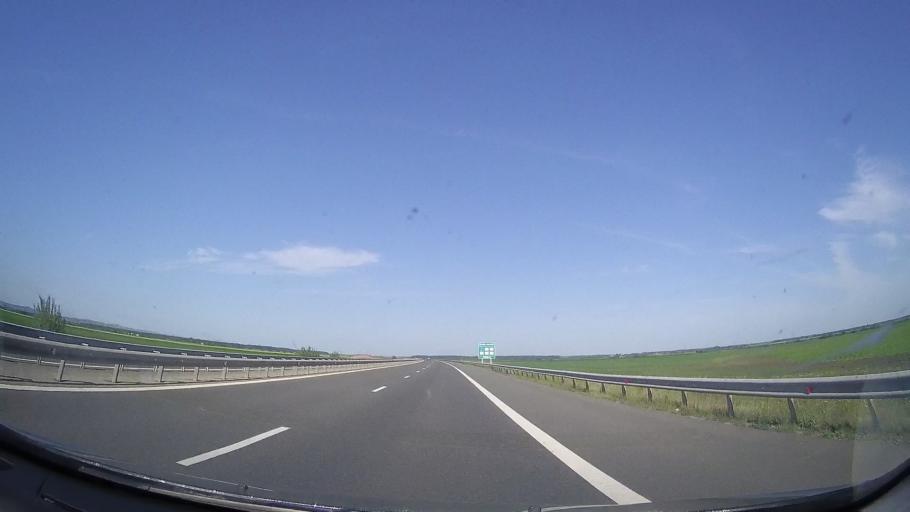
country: RO
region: Prahova
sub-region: Comuna Barcanesti
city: Barcanesti
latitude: 44.8797
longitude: 26.0663
